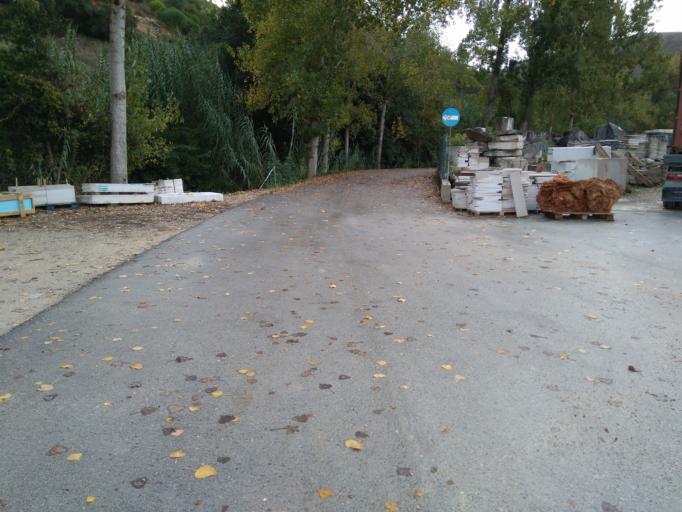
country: PT
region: Leiria
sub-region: Porto de Mos
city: Porto de Mos
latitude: 39.5841
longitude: -8.8194
